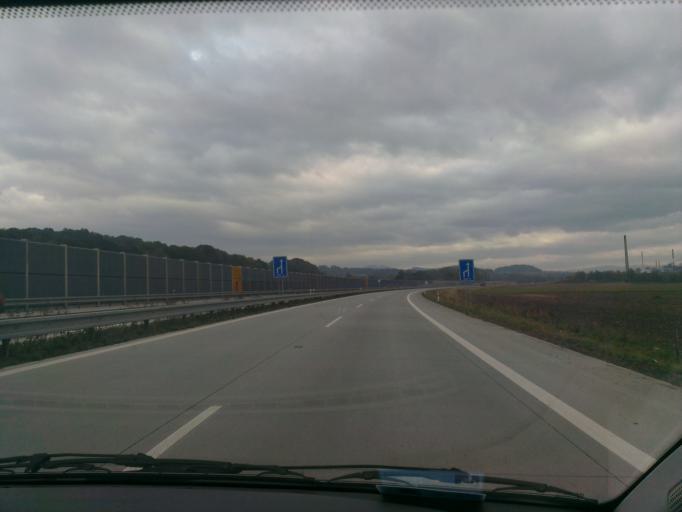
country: CZ
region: Zlin
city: Lesna
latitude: 49.5088
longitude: 17.9394
